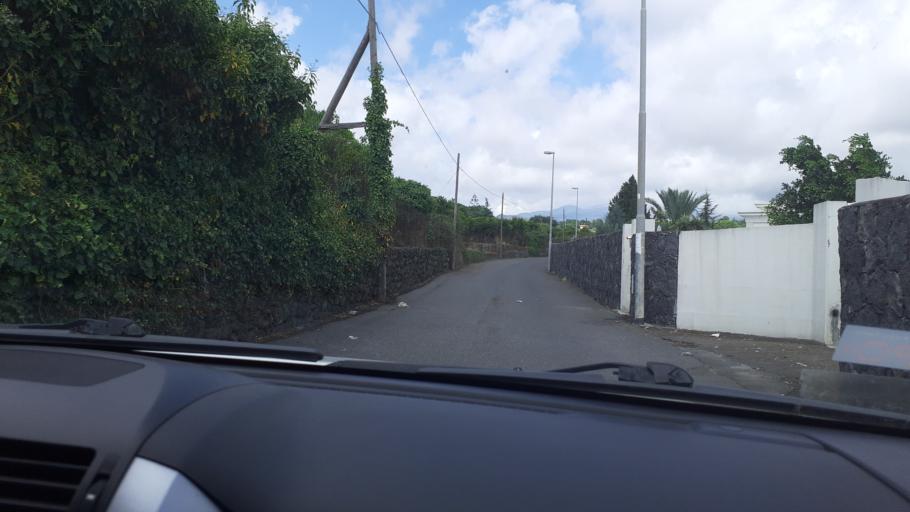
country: IT
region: Sicily
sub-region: Catania
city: San Giovanni la Punta
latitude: 37.5929
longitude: 15.0818
